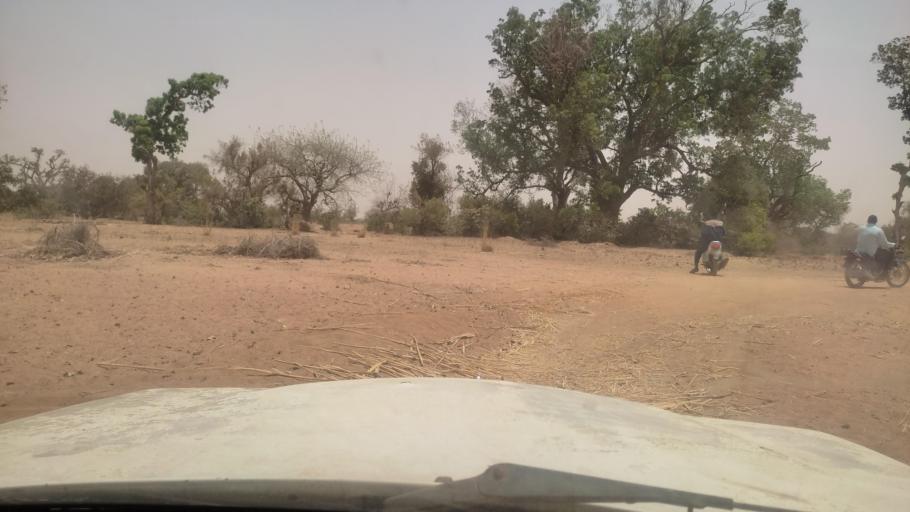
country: BF
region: Est
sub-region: Gnagna Province
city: Bogande
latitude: 13.0086
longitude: -0.0883
